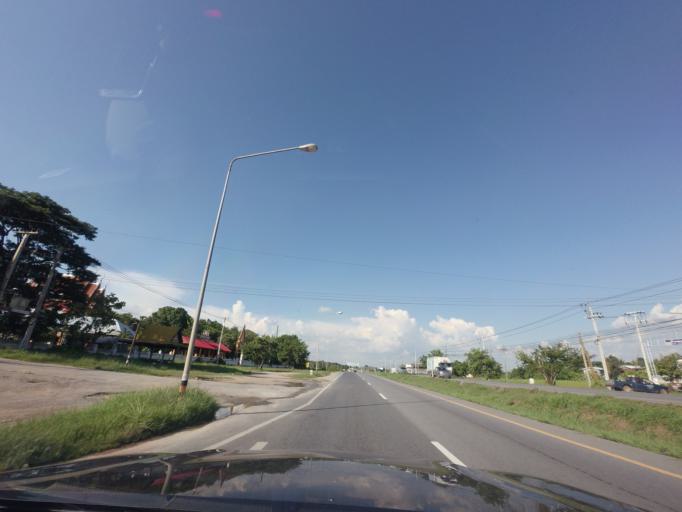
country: TH
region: Khon Kaen
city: Non Sila
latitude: 15.9519
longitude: 102.6838
